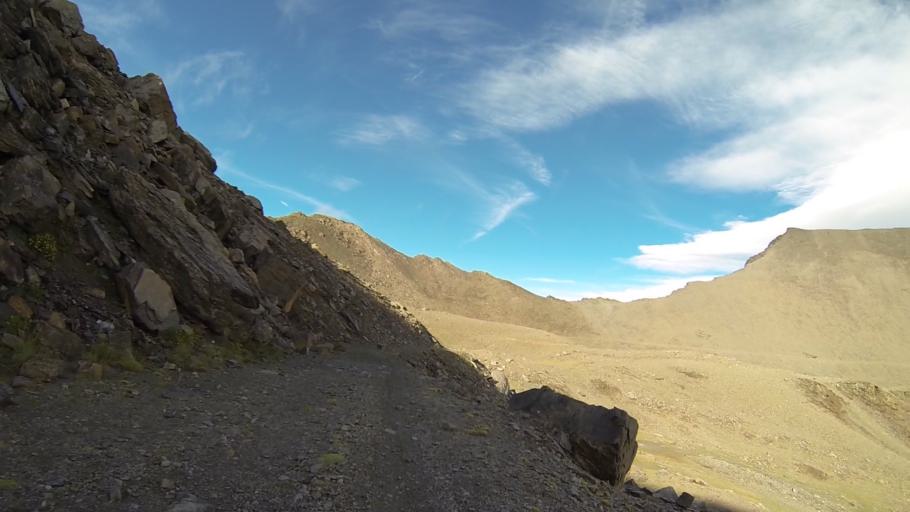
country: ES
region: Andalusia
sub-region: Provincia de Granada
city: Trevelez
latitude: 37.0511
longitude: -3.3292
